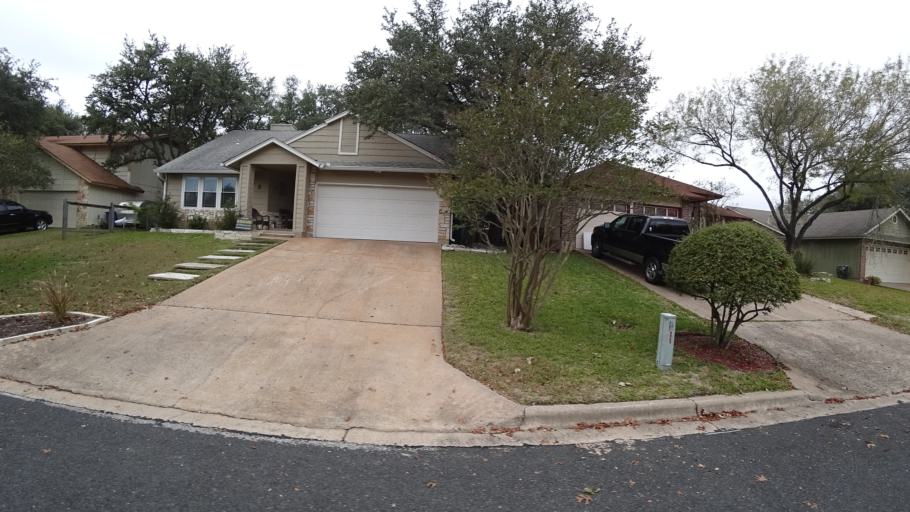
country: US
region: Texas
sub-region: Travis County
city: Barton Creek
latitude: 30.2412
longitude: -97.8980
